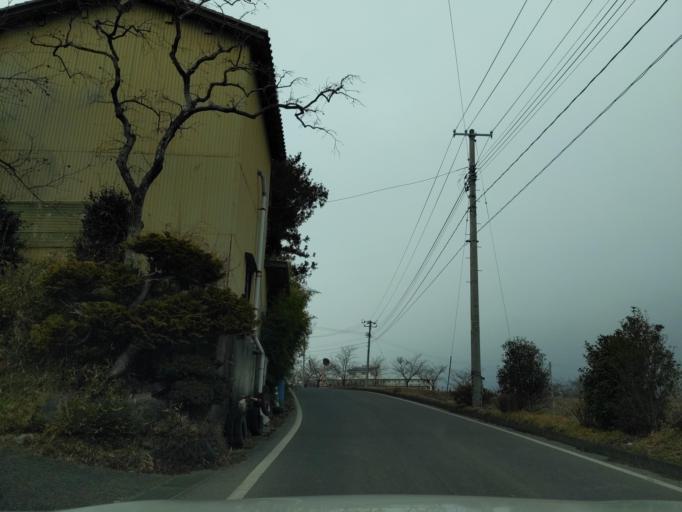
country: JP
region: Fukushima
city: Motomiya
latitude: 37.4557
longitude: 140.4145
